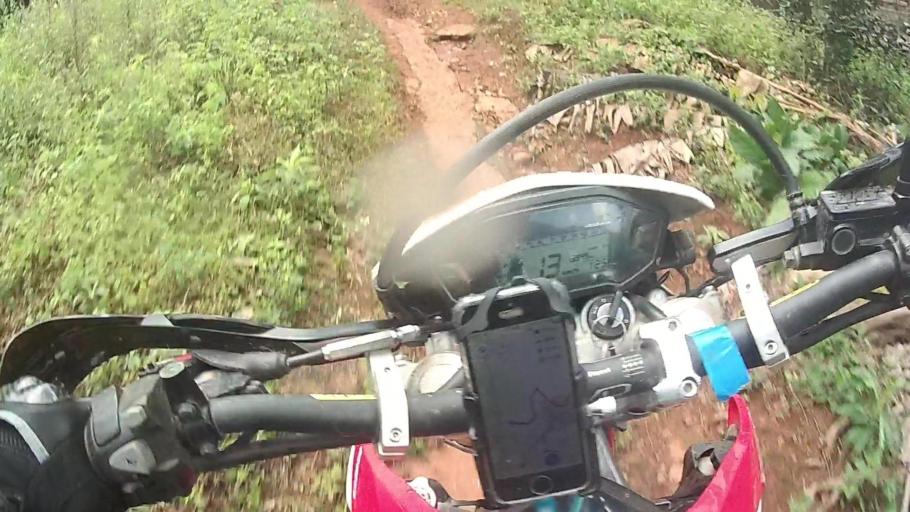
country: TH
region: Lampang
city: Wang Nuea
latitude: 19.0518
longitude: 99.4631
